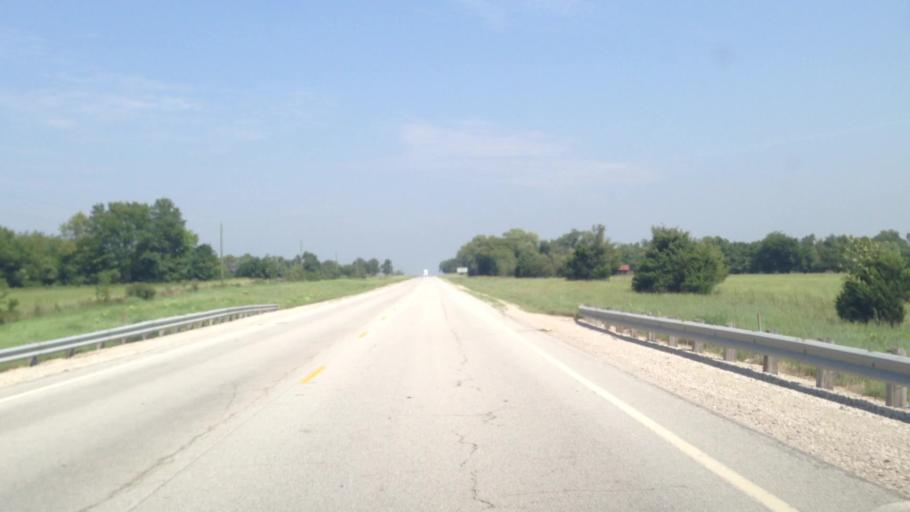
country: US
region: Kansas
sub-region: Labette County
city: Chetopa
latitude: 37.0068
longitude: -95.0857
